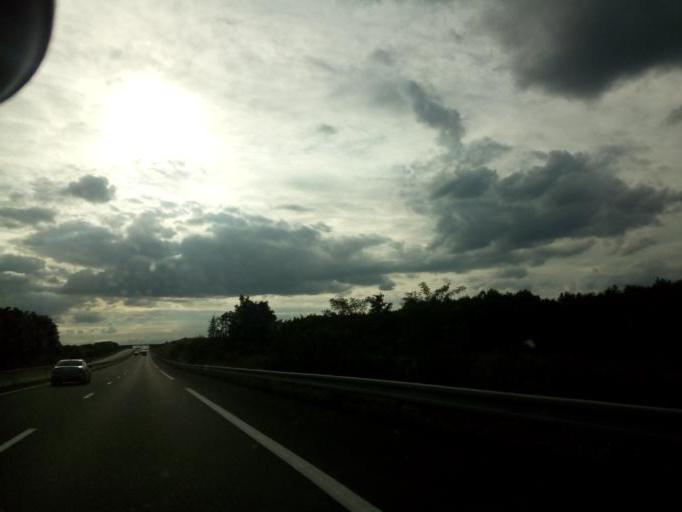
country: FR
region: Centre
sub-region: Departement du Loir-et-Cher
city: Saint-Georges-sur-Cher
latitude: 47.2950
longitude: 1.1448
